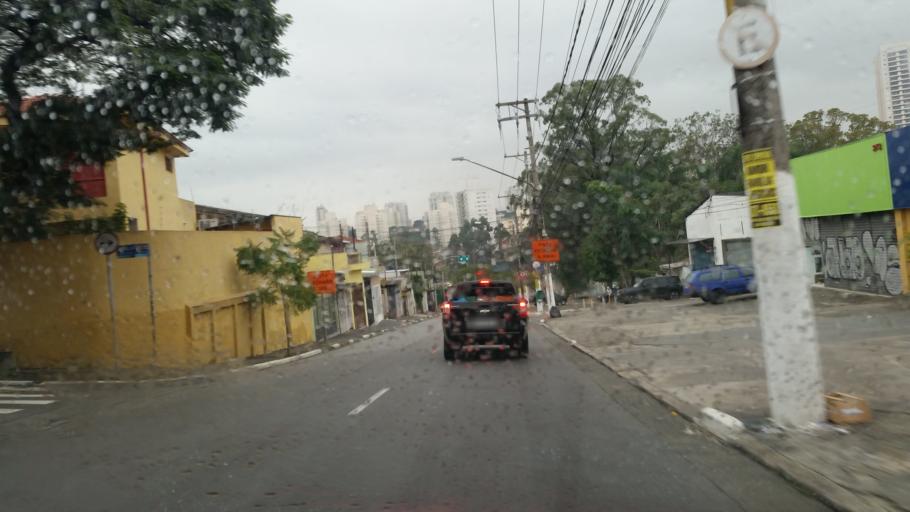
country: BR
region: Sao Paulo
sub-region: Diadema
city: Diadema
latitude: -23.6359
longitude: -46.6610
